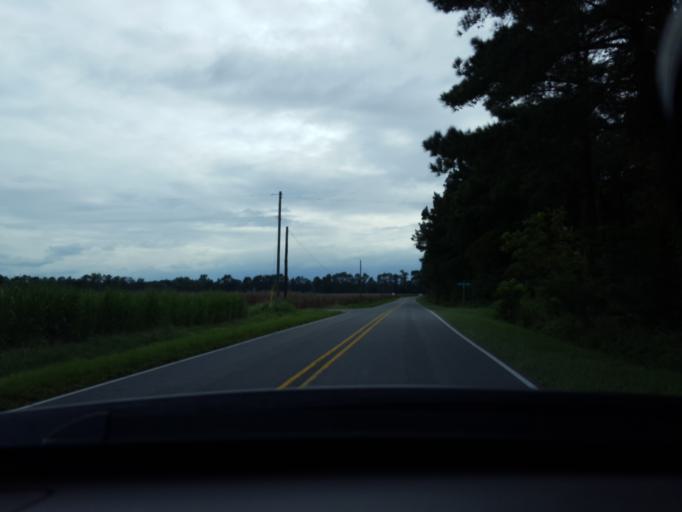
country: US
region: North Carolina
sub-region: Duplin County
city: Rose Hill
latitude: 34.9080
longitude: -78.0388
